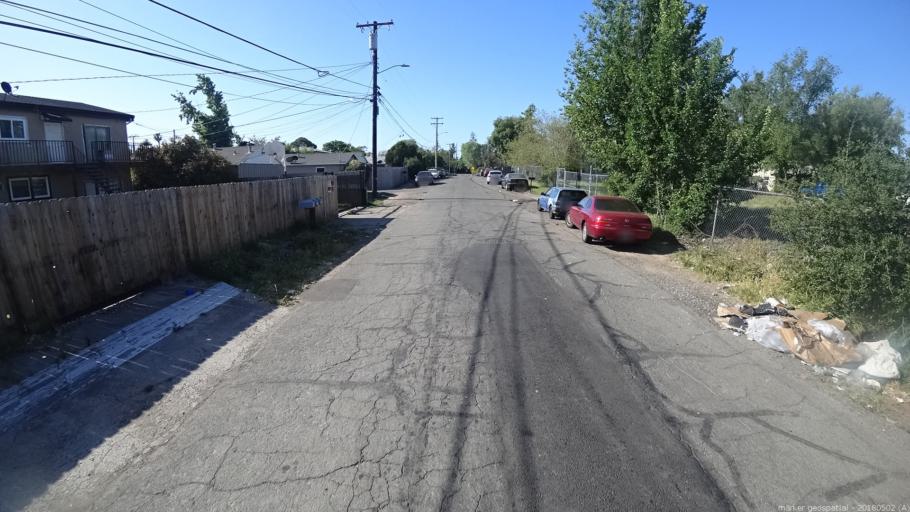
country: US
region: California
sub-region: Sacramento County
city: Arden-Arcade
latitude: 38.6103
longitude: -121.4213
